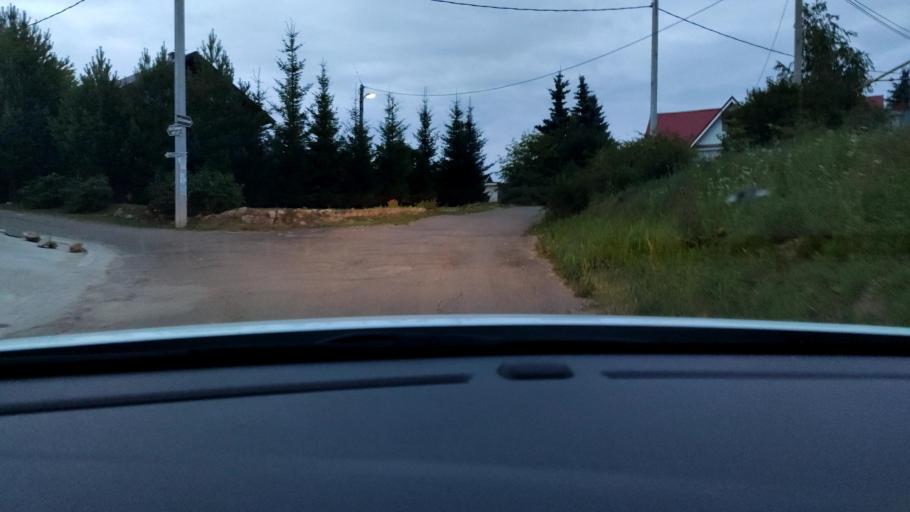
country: RU
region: Tatarstan
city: Stolbishchi
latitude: 55.7429
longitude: 49.2681
